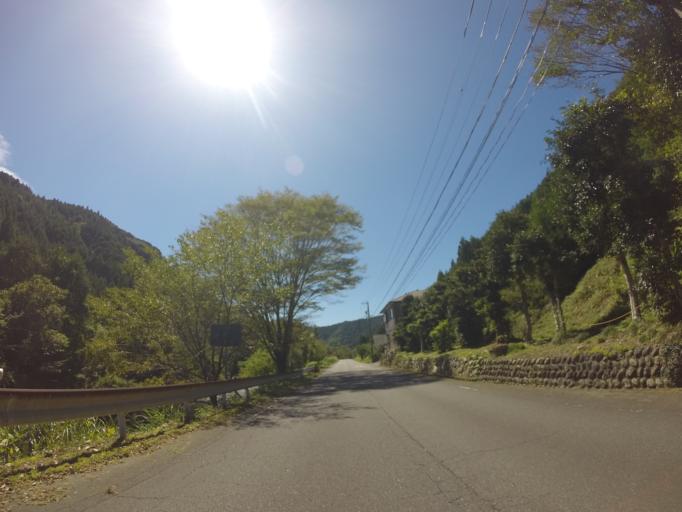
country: JP
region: Shizuoka
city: Fujieda
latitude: 34.9622
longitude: 138.2117
